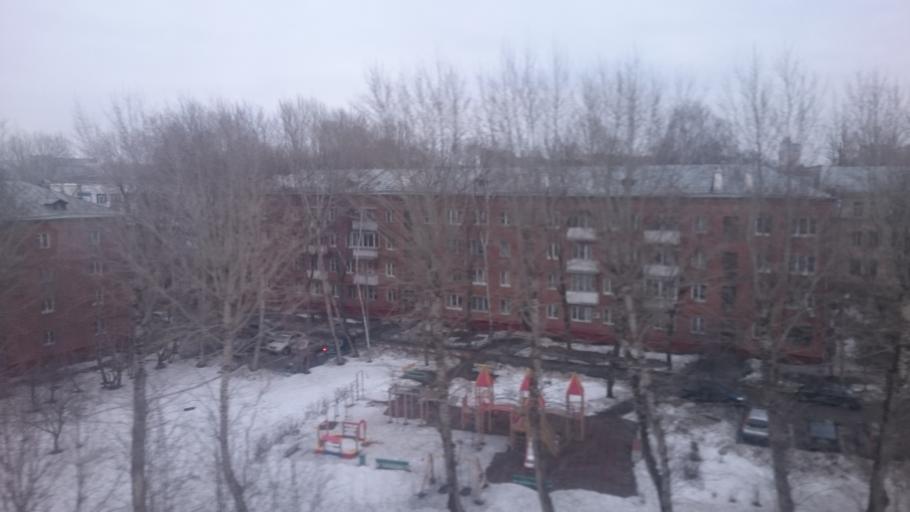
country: RU
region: Moscow
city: Pokrovskoye-Streshnevo
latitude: 55.8167
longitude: 37.4465
